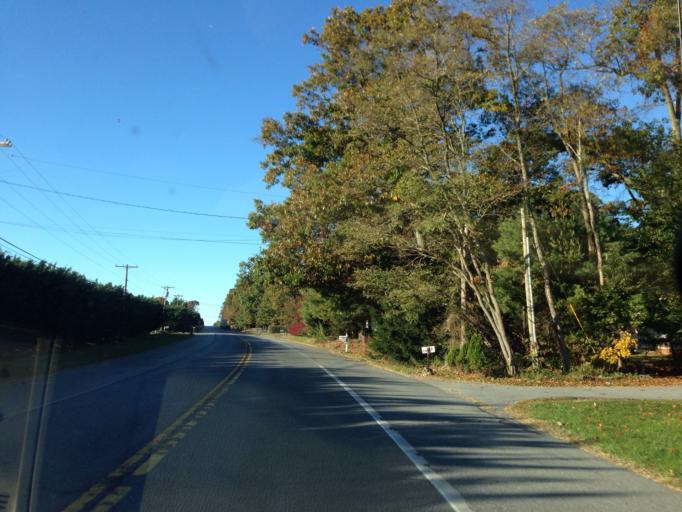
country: US
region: Maryland
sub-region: Carroll County
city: Mount Airy
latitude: 39.4411
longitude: -77.1002
